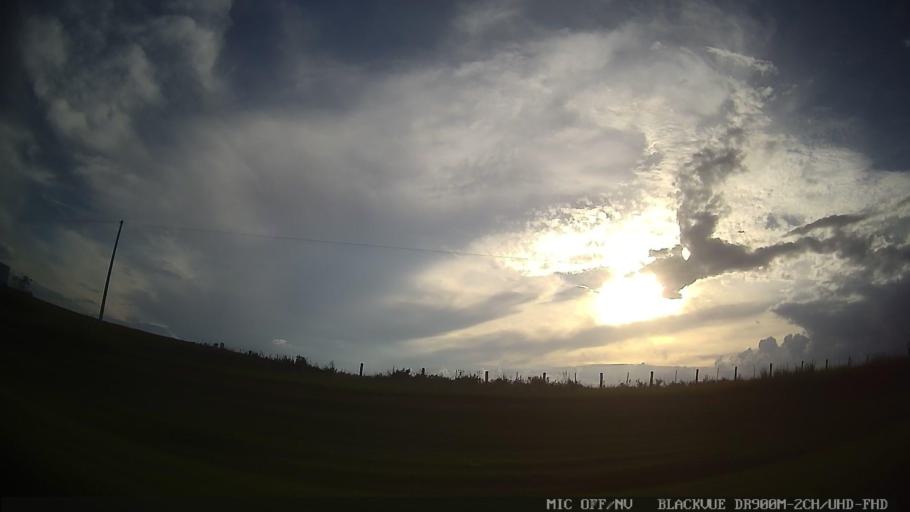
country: BR
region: Sao Paulo
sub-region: Tiete
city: Tiete
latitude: -23.1294
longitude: -47.6958
